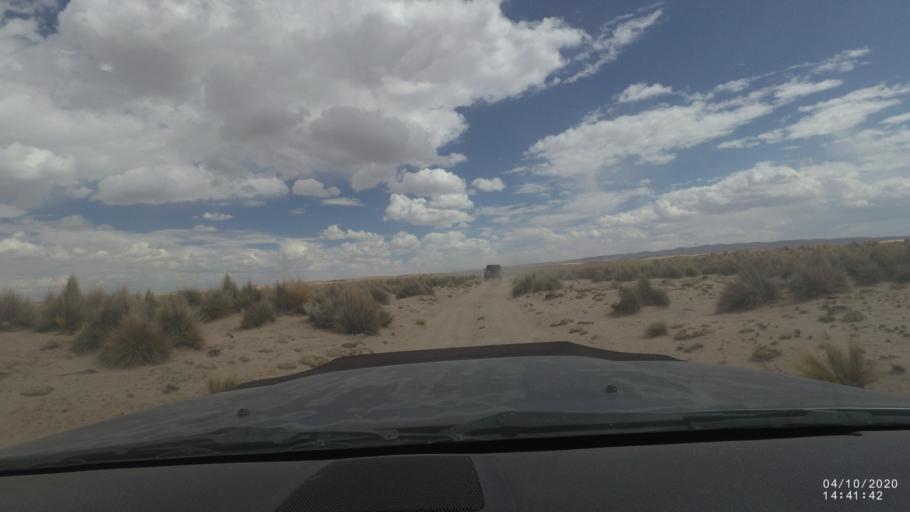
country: BO
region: Oruro
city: Poopo
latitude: -18.6835
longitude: -67.4906
